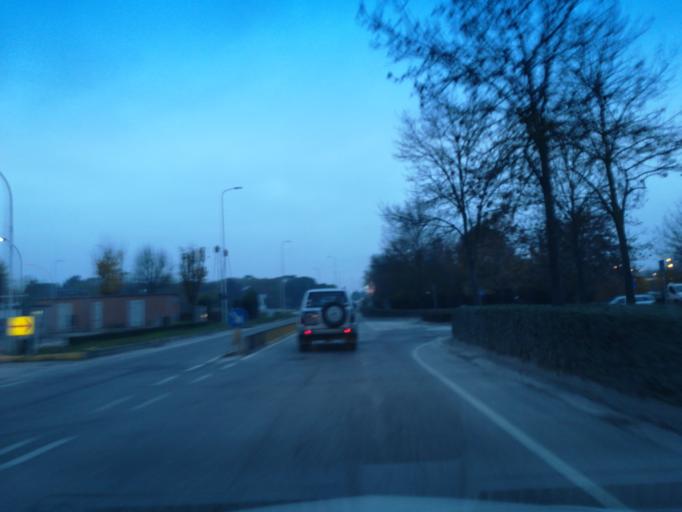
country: IT
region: Emilia-Romagna
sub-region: Provincia di Ravenna
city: Faenza
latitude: 44.2954
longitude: 11.8596
